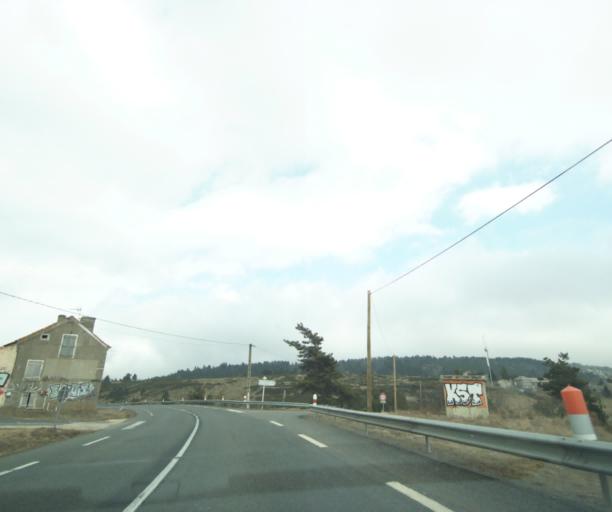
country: FR
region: Languedoc-Roussillon
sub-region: Departement de la Lozere
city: Langogne
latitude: 44.6476
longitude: 3.7308
